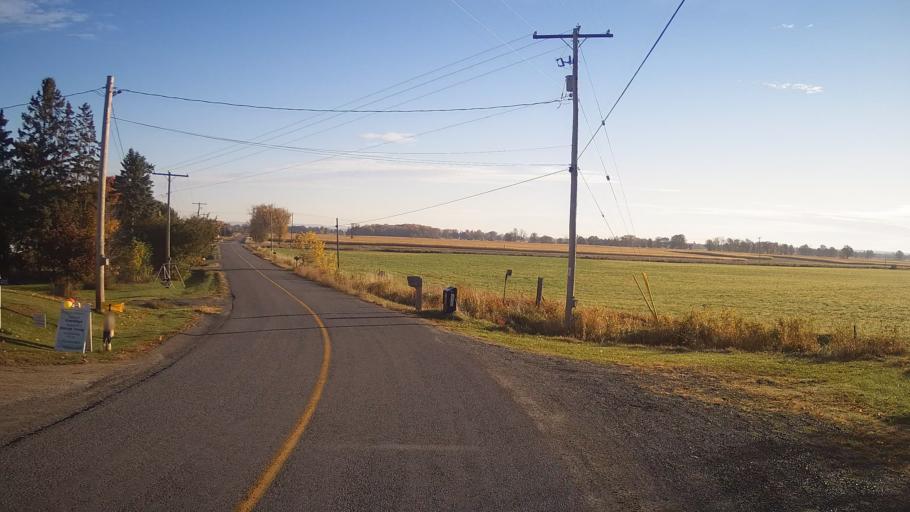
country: CA
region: Ontario
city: Arnprior
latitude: 45.3451
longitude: -76.3204
